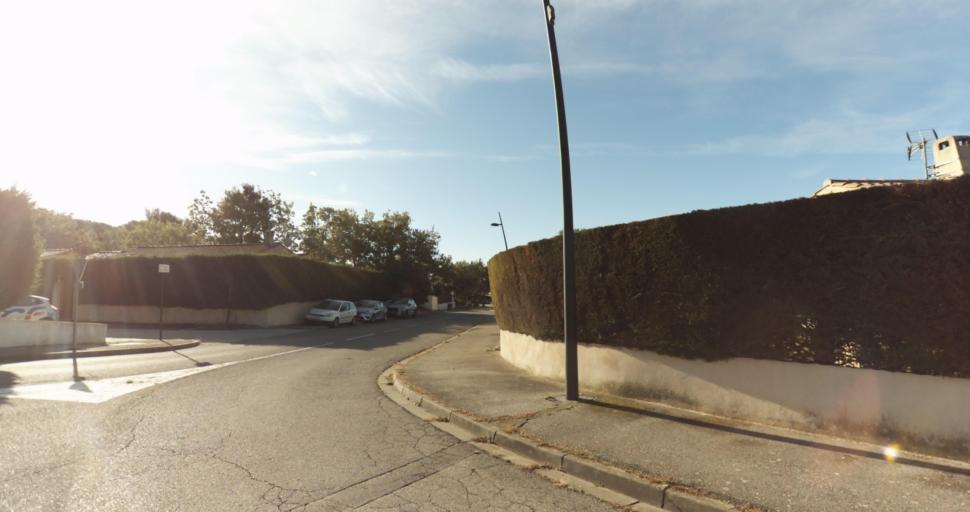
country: FR
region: Provence-Alpes-Cote d'Azur
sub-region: Departement des Bouches-du-Rhone
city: Venelles
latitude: 43.5960
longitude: 5.4715
